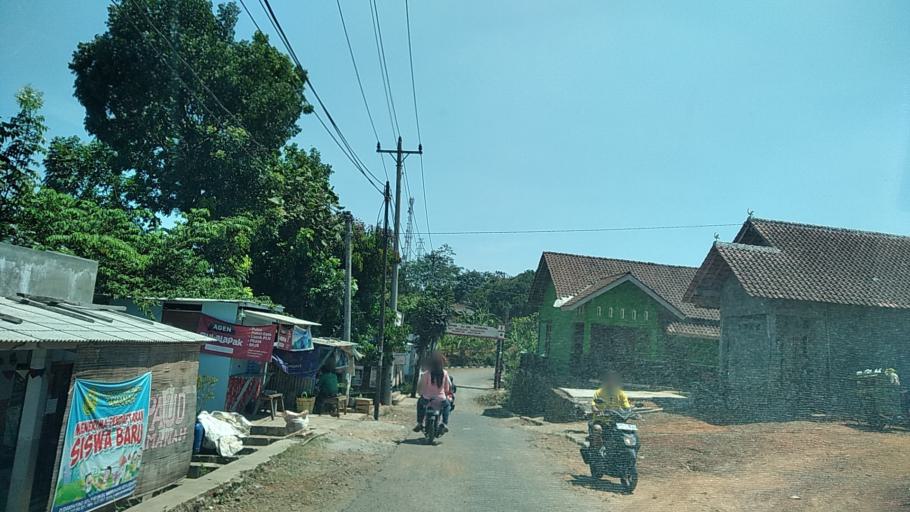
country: ID
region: Central Java
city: Ungaran
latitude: -7.0997
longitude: 110.4128
